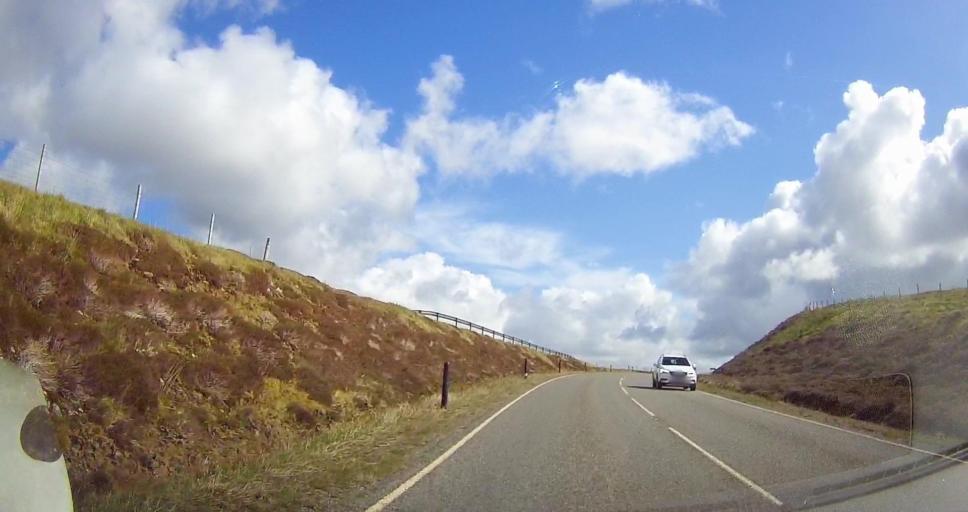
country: GB
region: Scotland
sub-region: Shetland Islands
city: Lerwick
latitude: 60.4562
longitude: -1.3972
